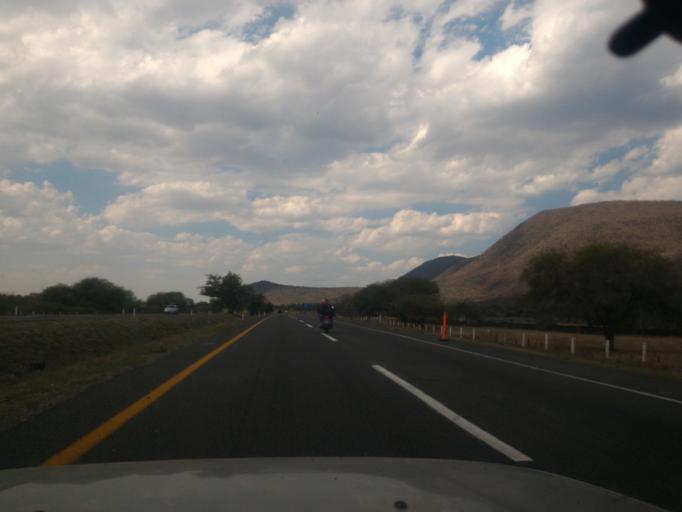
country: MX
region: Jalisco
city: Zacoalco de Torres
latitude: 20.1764
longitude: -103.5093
